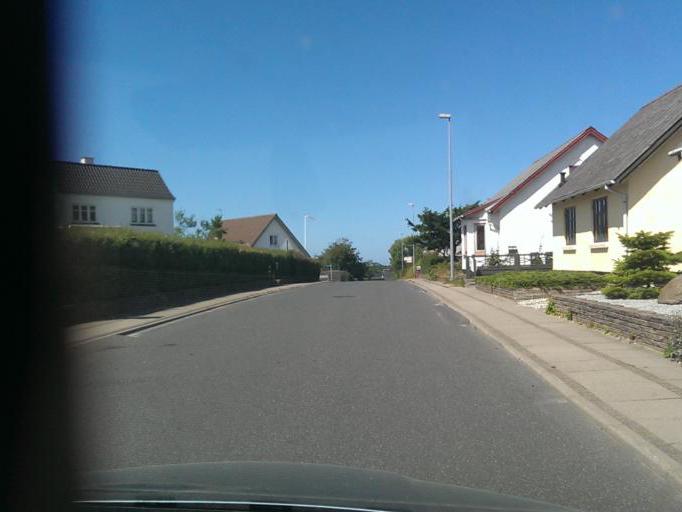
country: DK
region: North Denmark
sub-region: Jammerbugt Kommune
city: Pandrup
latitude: 57.3134
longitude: 9.7140
